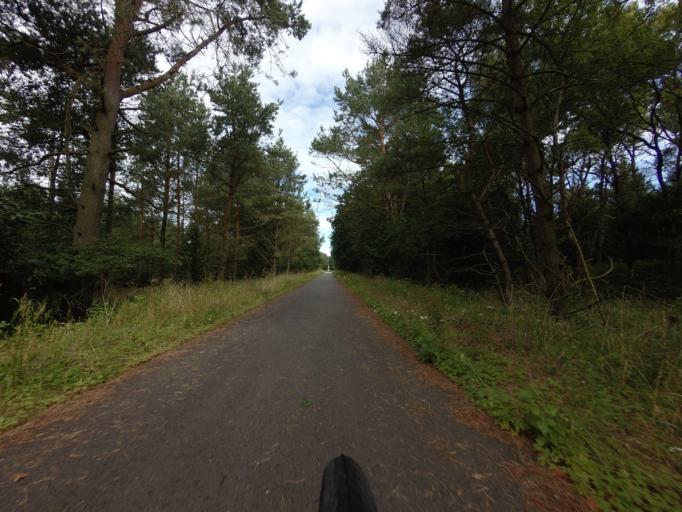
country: DK
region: Central Jutland
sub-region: Norddjurs Kommune
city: Auning
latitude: 56.4065
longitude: 10.3975
